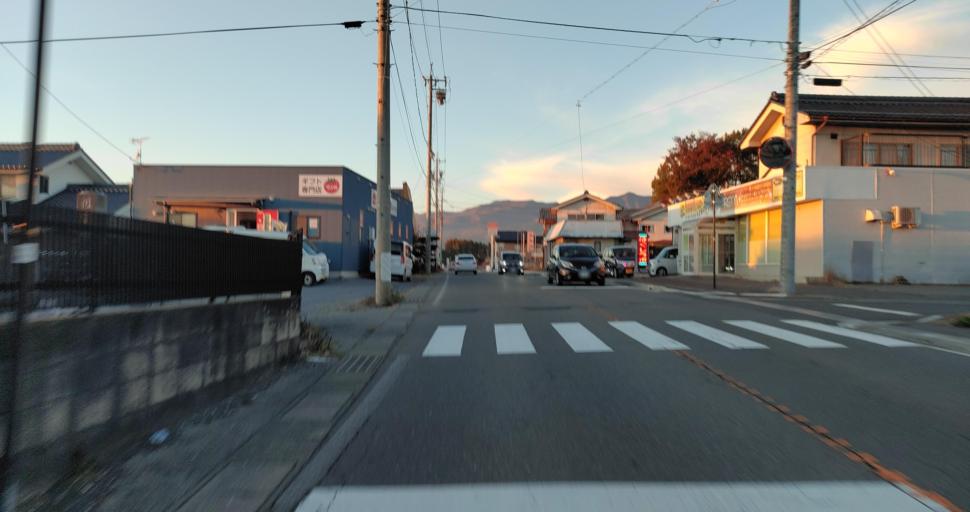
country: JP
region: Nagano
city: Komoro
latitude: 36.2909
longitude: 138.4601
